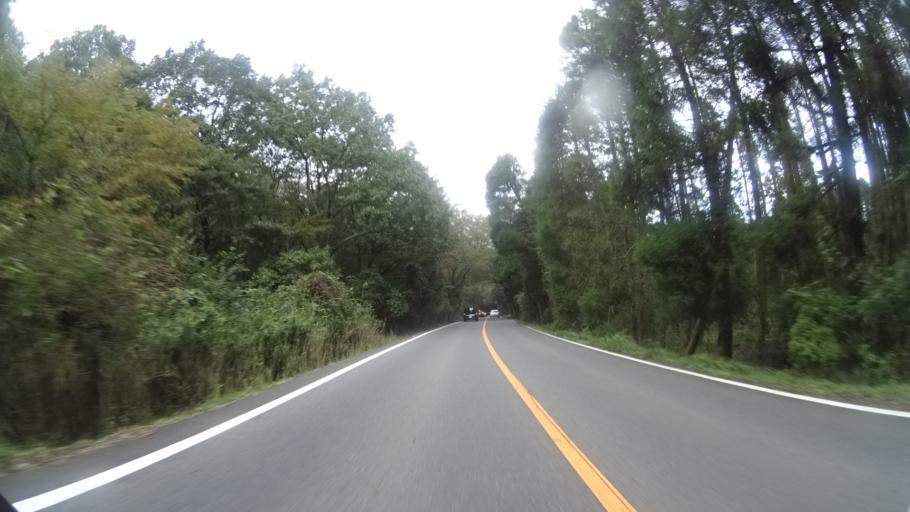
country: JP
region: Oita
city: Beppu
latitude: 33.2703
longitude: 131.4081
